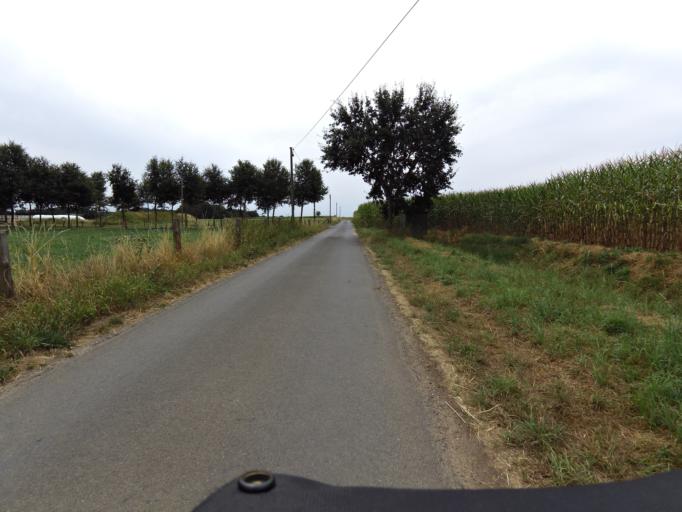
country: DE
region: North Rhine-Westphalia
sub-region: Regierungsbezirk Dusseldorf
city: Weeze
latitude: 51.5862
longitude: 6.1842
